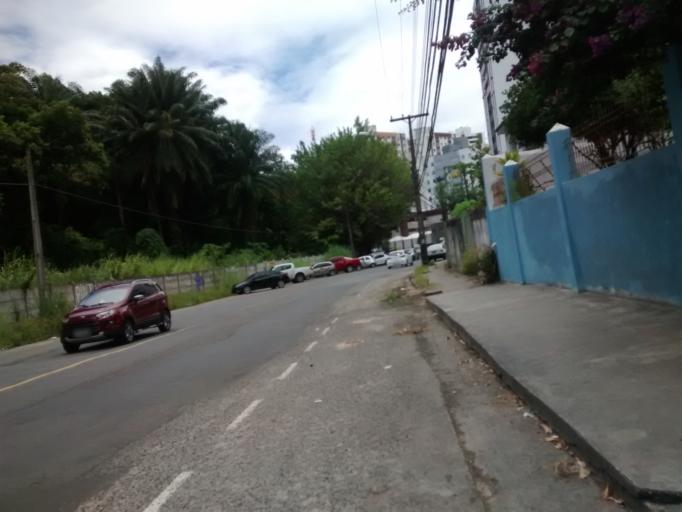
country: BR
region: Bahia
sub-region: Salvador
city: Salvador
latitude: -12.9741
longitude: -38.4407
